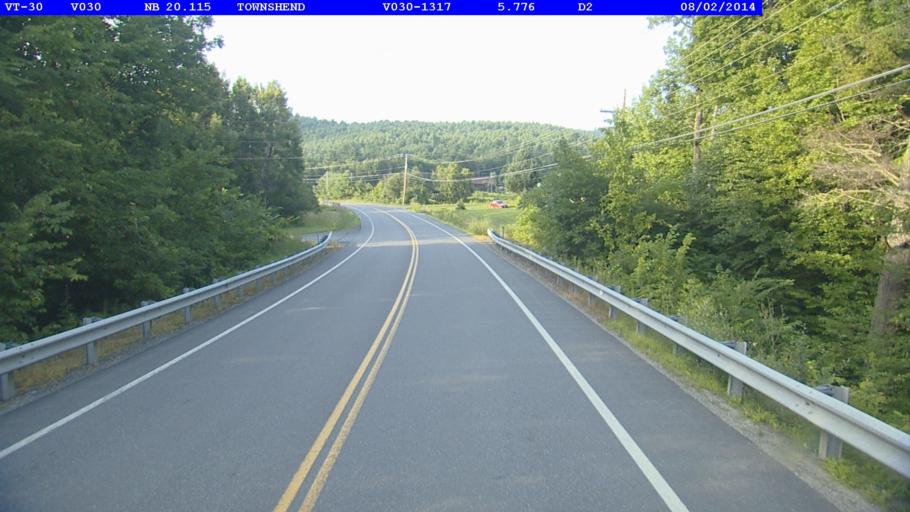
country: US
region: Vermont
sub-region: Windham County
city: Newfane
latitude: 43.0755
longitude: -72.7043
